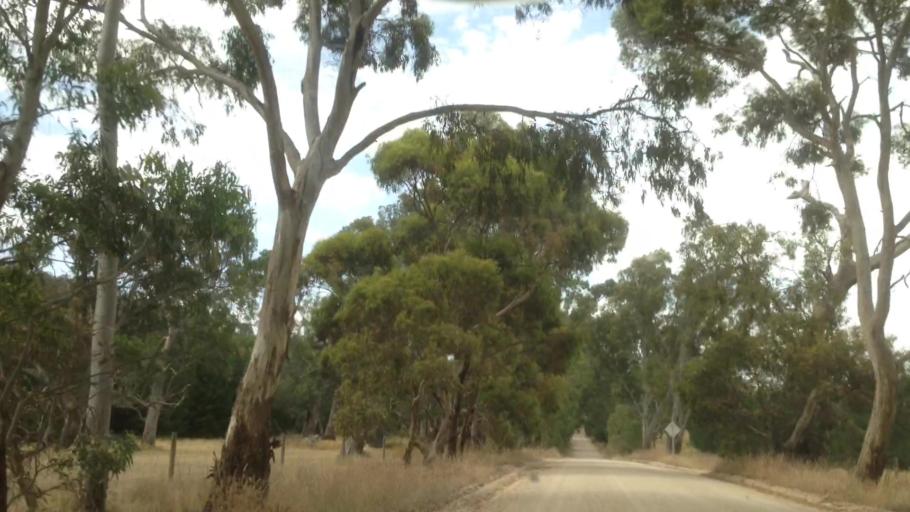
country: AU
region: South Australia
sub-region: Barossa
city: Williamstown
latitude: -34.6874
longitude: 138.9705
